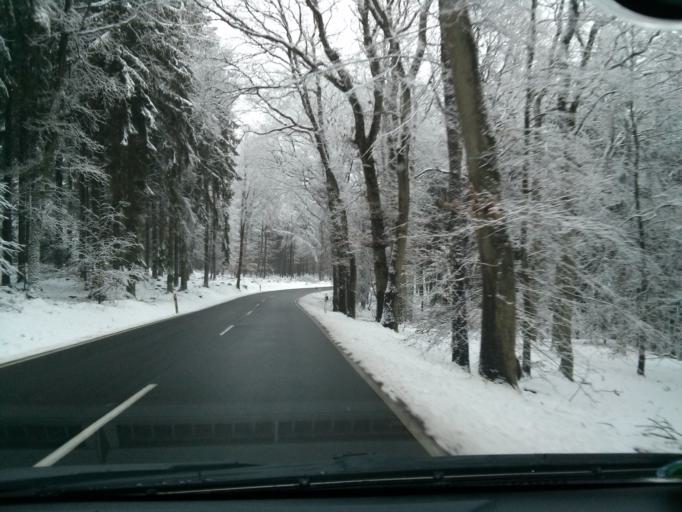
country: DE
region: Rheinland-Pfalz
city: Kirchsahr
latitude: 50.5235
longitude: 6.8316
